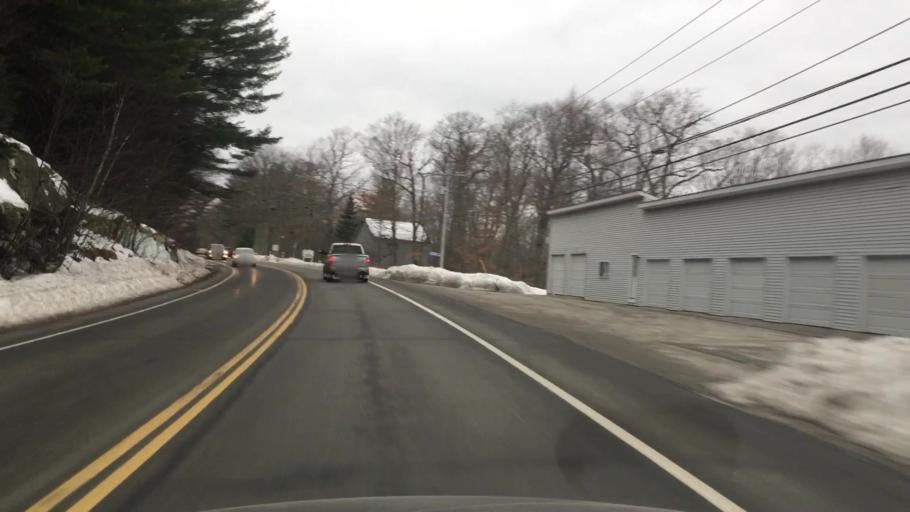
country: US
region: New Hampshire
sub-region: Merrimack County
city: Newbury
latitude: 43.3405
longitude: -72.0597
